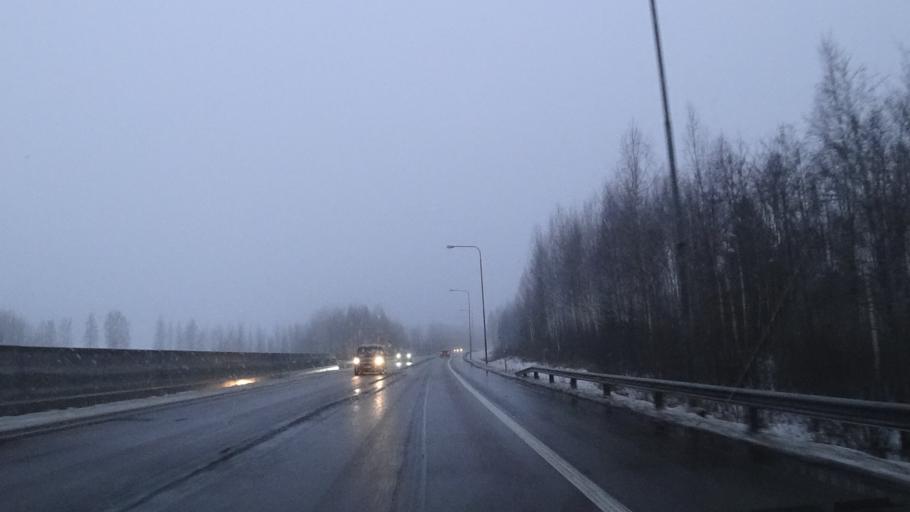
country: FI
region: Paijanne Tavastia
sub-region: Lahti
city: Hollola
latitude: 60.9815
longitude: 25.4695
